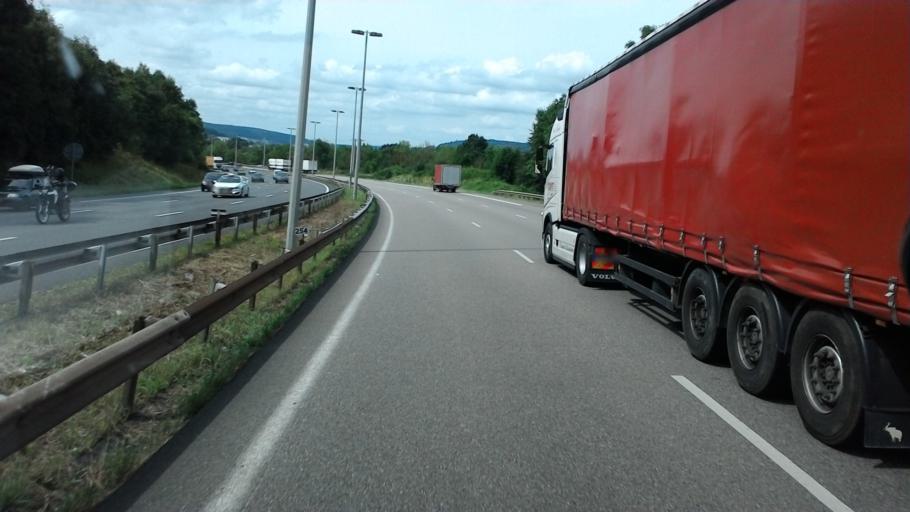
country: FR
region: Lorraine
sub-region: Departement de Meurthe-et-Moselle
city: Champigneulles
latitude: 48.7253
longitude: 6.1695
